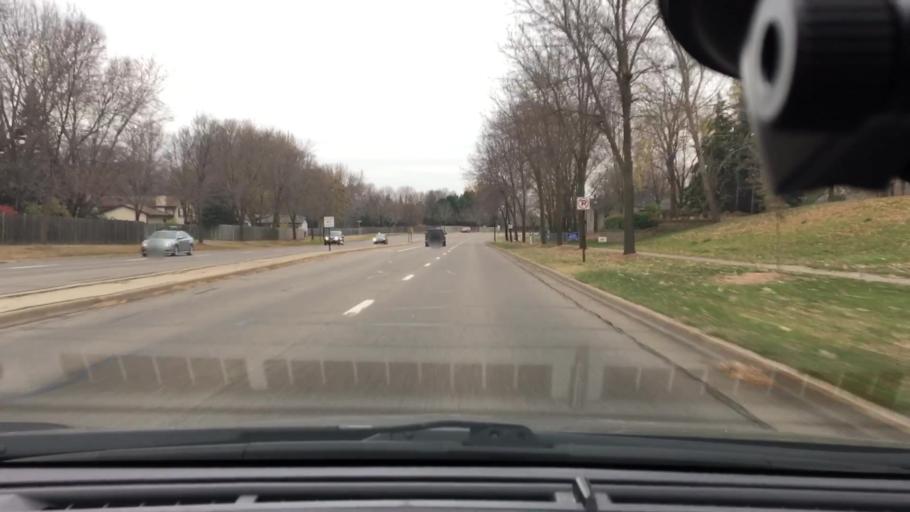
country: US
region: Minnesota
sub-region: Hennepin County
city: Maple Grove
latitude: 45.1125
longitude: -93.4517
